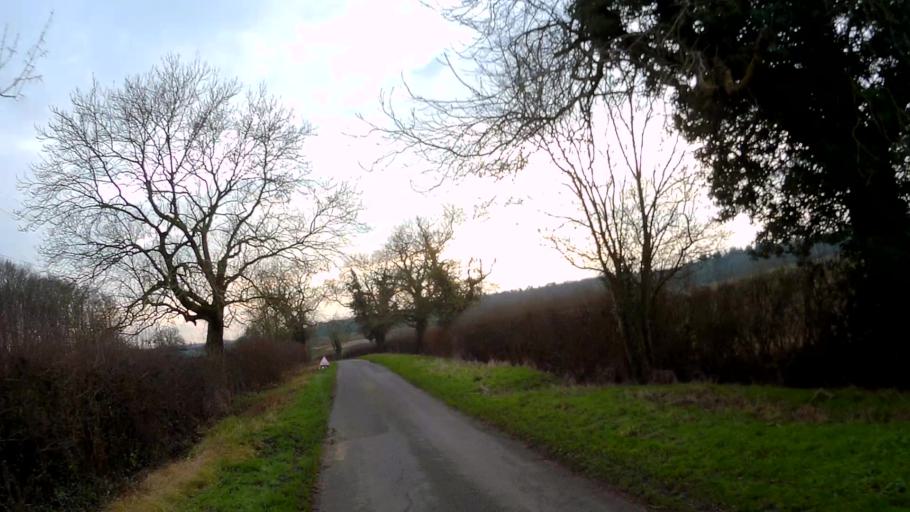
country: GB
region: England
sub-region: Lincolnshire
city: Bourne
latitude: 52.8234
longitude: -0.4060
